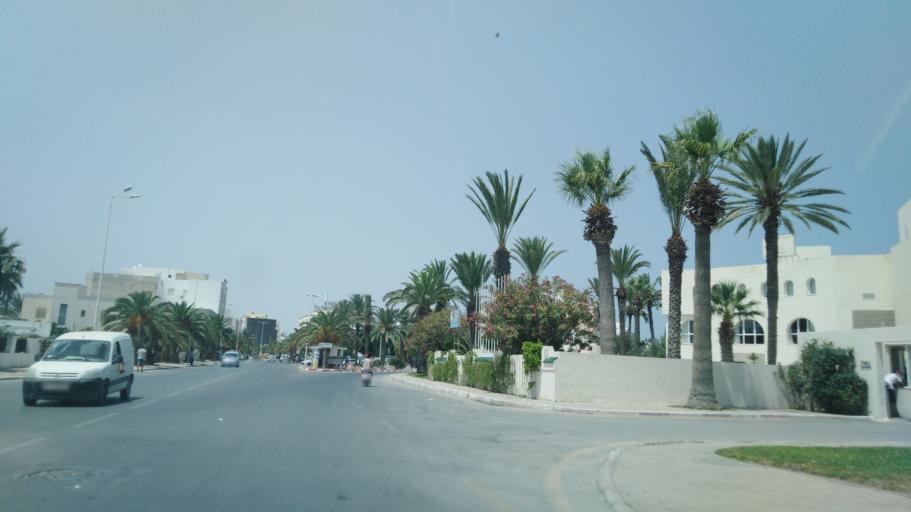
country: TN
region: Al Mahdiyah
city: Mahdia
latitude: 35.5168
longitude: 11.0443
